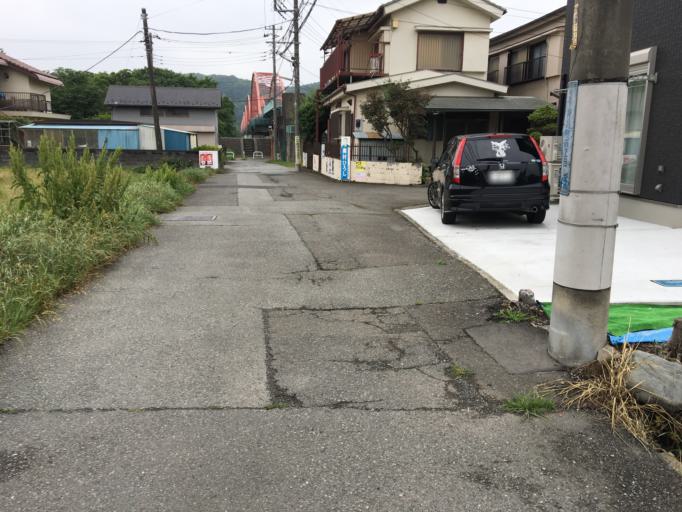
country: JP
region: Tokyo
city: Fussa
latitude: 35.7047
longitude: 139.3400
